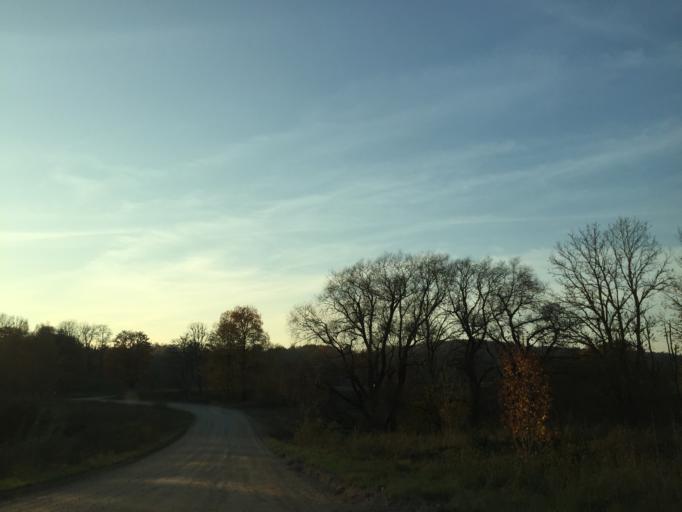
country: LV
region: Vainode
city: Vainode
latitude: 56.5059
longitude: 21.8187
